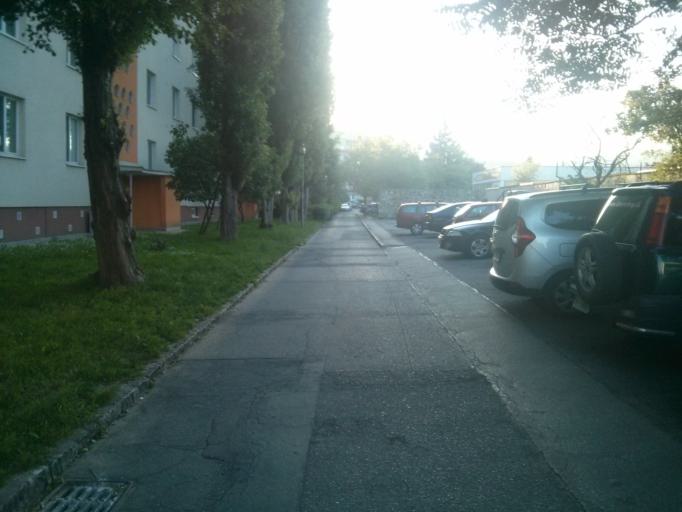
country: SK
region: Bratislavsky
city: Bratislava
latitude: 48.1722
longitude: 17.1339
